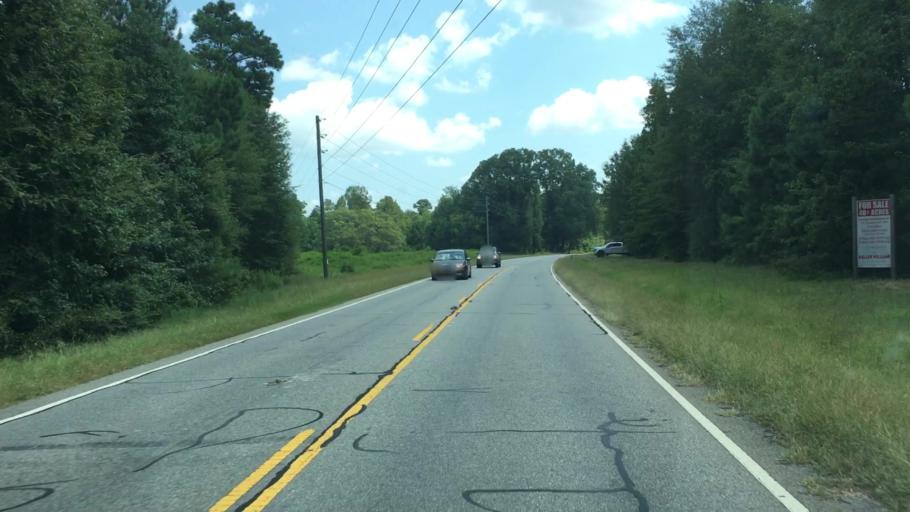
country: US
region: Georgia
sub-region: Oconee County
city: Bogart
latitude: 33.8905
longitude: -83.5614
